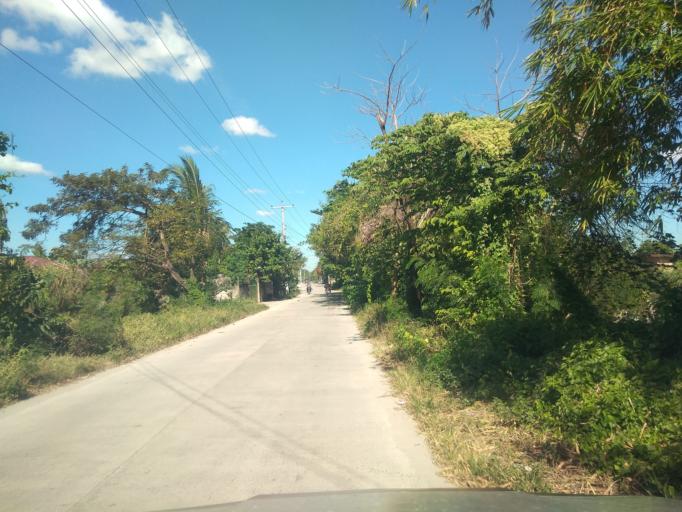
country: PH
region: Central Luzon
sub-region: Province of Pampanga
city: Bacolor
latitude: 15.0050
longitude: 120.6425
